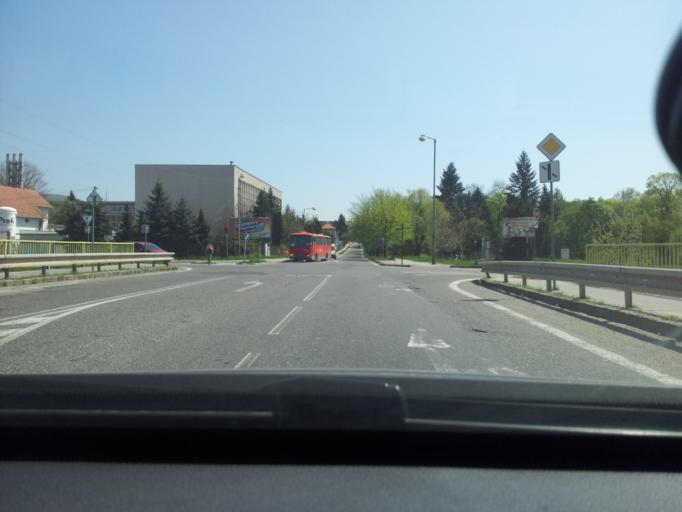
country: SK
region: Nitriansky
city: Zlate Moravce
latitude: 48.3831
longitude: 18.3887
